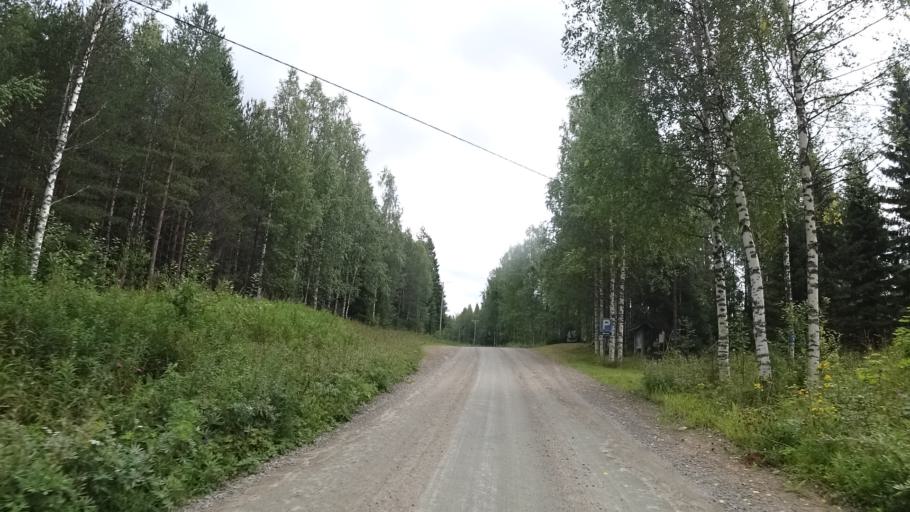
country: FI
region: North Karelia
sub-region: Joensuu
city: Ilomantsi
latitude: 62.9306
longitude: 31.3126
